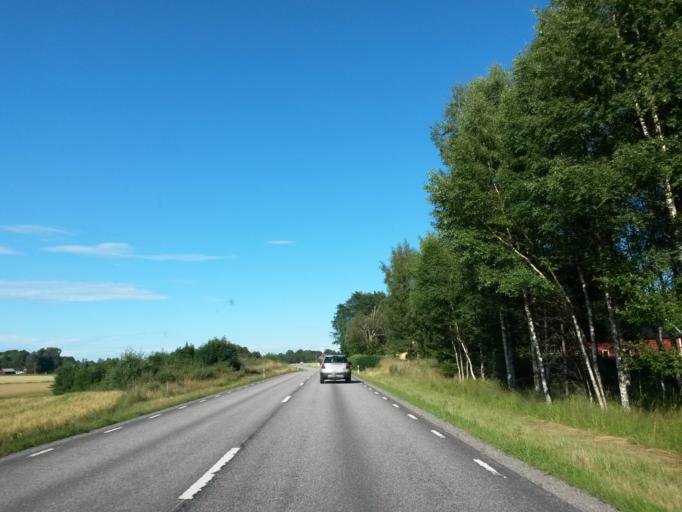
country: SE
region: Vaestra Goetaland
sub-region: Grastorps Kommun
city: Graestorp
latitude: 58.3760
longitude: 12.7338
